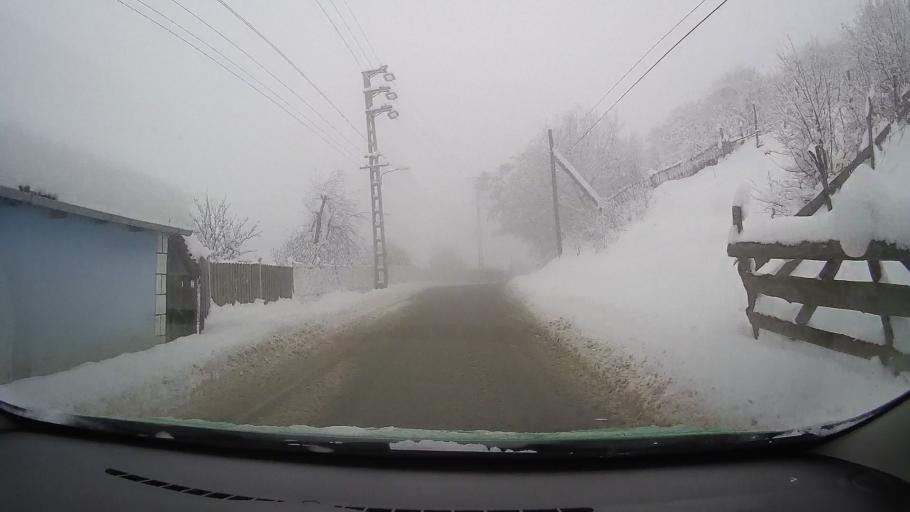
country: RO
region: Sibiu
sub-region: Comuna Poiana Sibiului
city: Poiana Sibiului
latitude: 45.8040
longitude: 23.7747
